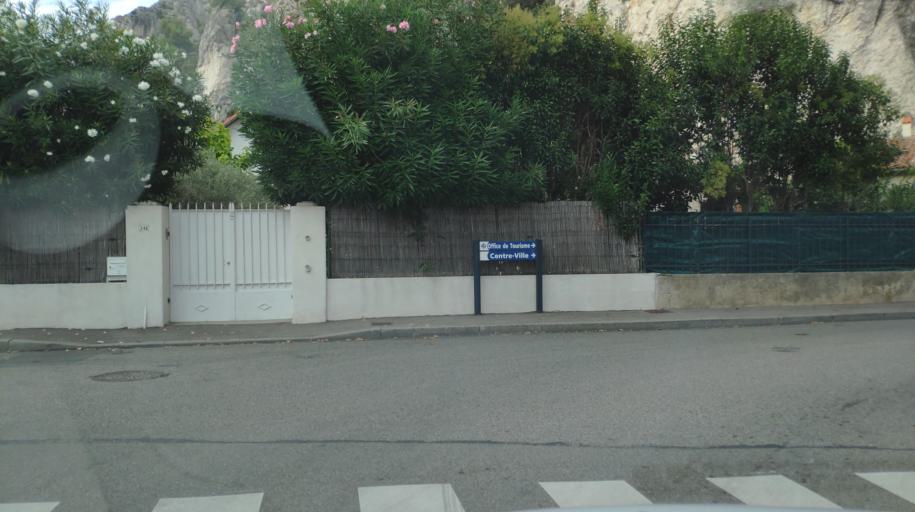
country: FR
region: Provence-Alpes-Cote d'Azur
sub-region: Departement du Vaucluse
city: Cavaillon
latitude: 43.8327
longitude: 5.0325
